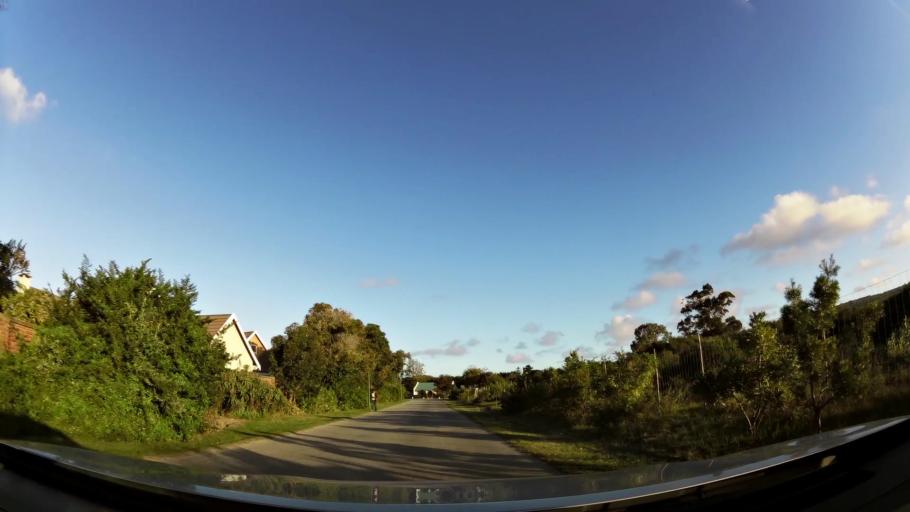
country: ZA
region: Western Cape
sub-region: Eden District Municipality
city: Knysna
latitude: -34.0114
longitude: 22.7792
